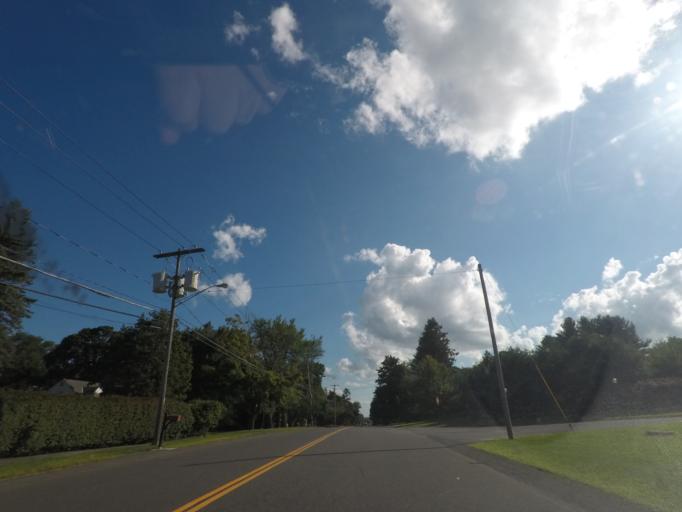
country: US
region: New York
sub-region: Albany County
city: Menands
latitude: 42.6760
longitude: -73.7441
